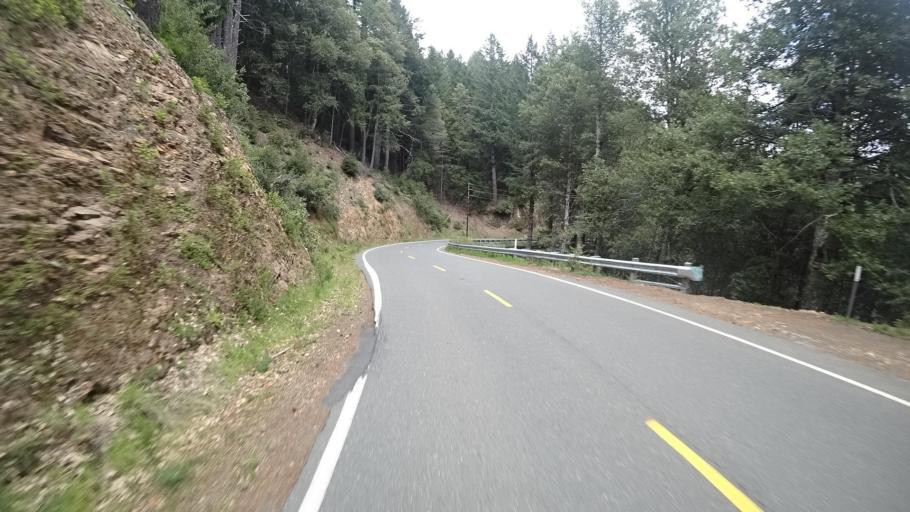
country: US
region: California
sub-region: Humboldt County
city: Redway
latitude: 40.0481
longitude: -124.0207
